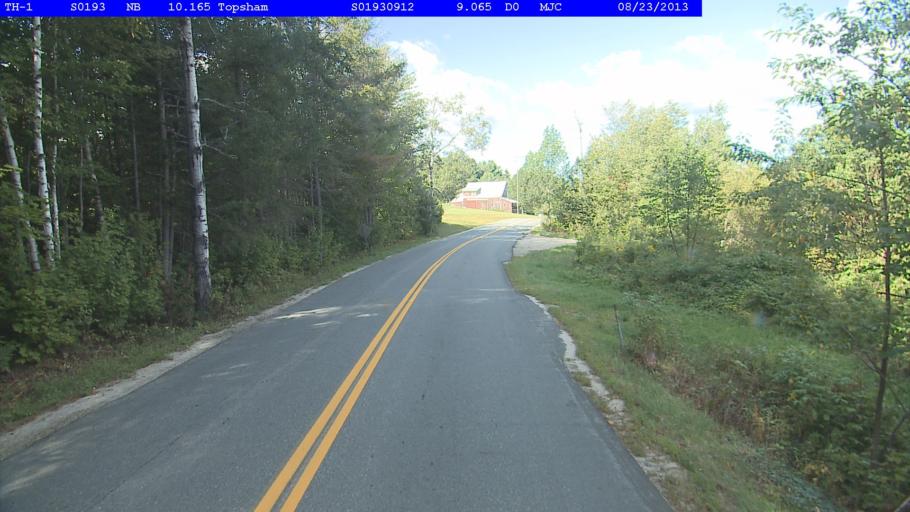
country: US
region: New Hampshire
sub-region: Grafton County
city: Woodsville
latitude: 44.1886
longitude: -72.2216
